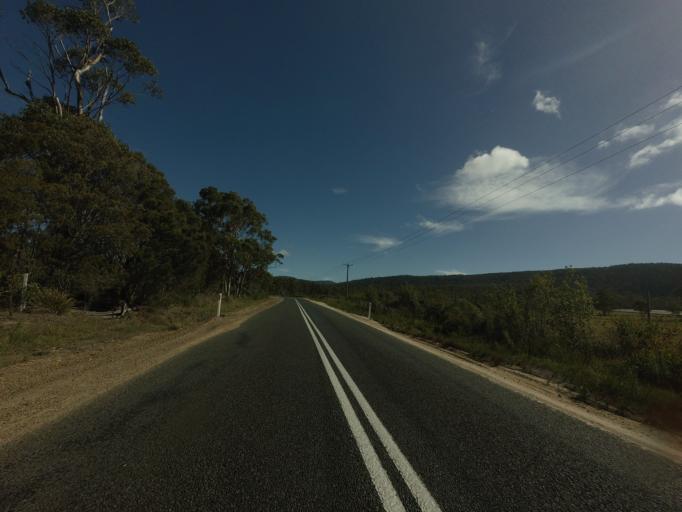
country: AU
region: Tasmania
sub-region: Break O'Day
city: St Helens
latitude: -41.8337
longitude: 148.2556
